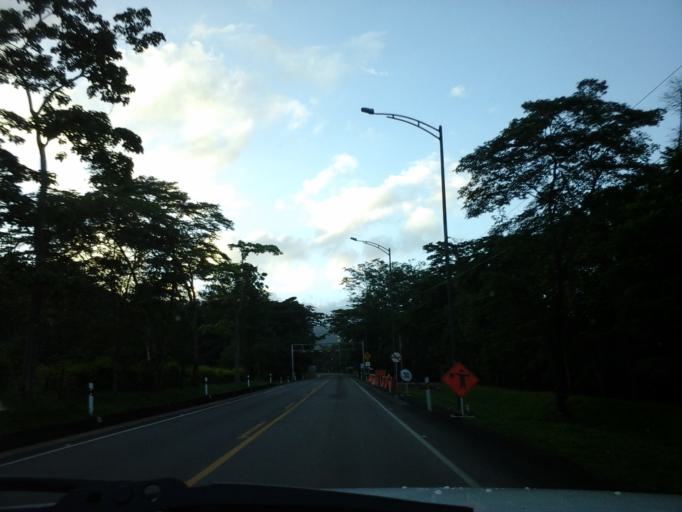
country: CO
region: Meta
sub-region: Villavicencio
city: Villavicencio
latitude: 4.1363
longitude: -73.6559
